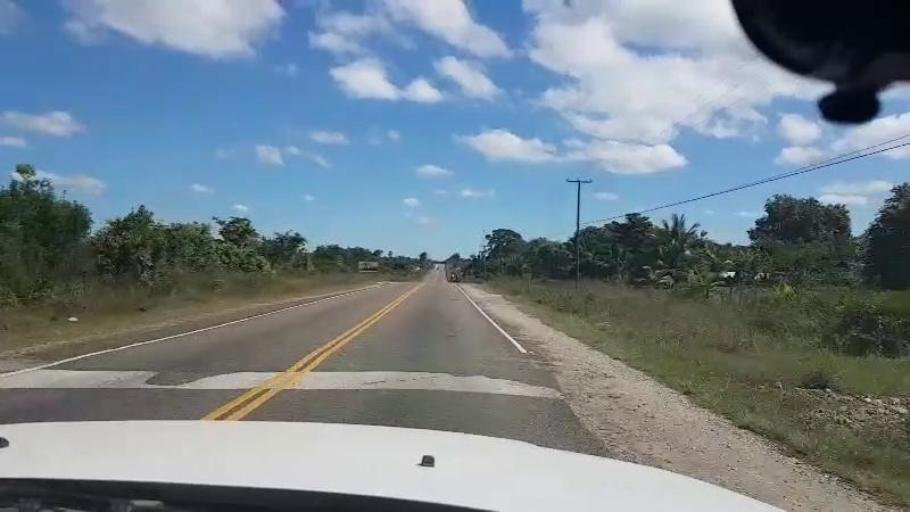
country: BZ
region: Cayo
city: Belmopan
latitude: 17.2771
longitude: -88.6712
